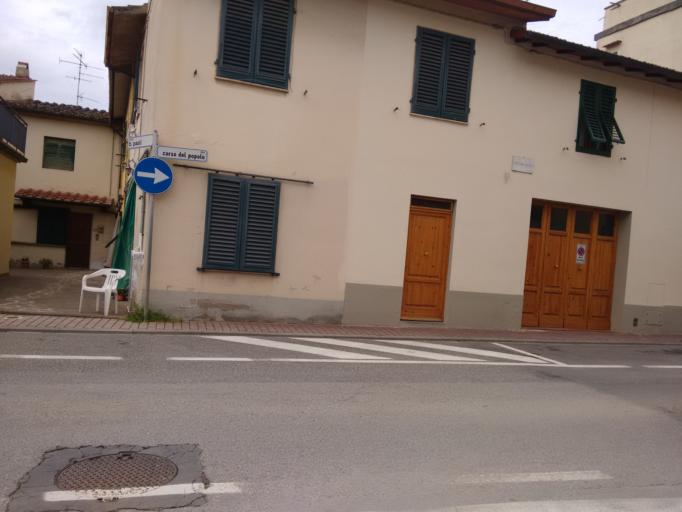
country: IT
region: Tuscany
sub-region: Province of Florence
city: Strada in Chianti
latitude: 43.6597
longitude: 11.2963
